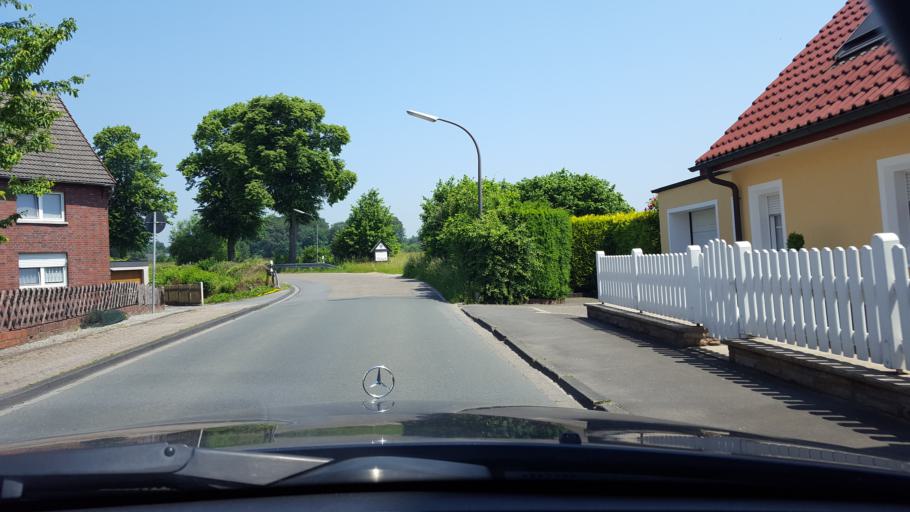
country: DE
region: North Rhine-Westphalia
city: Olfen
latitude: 51.7008
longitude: 7.3106
